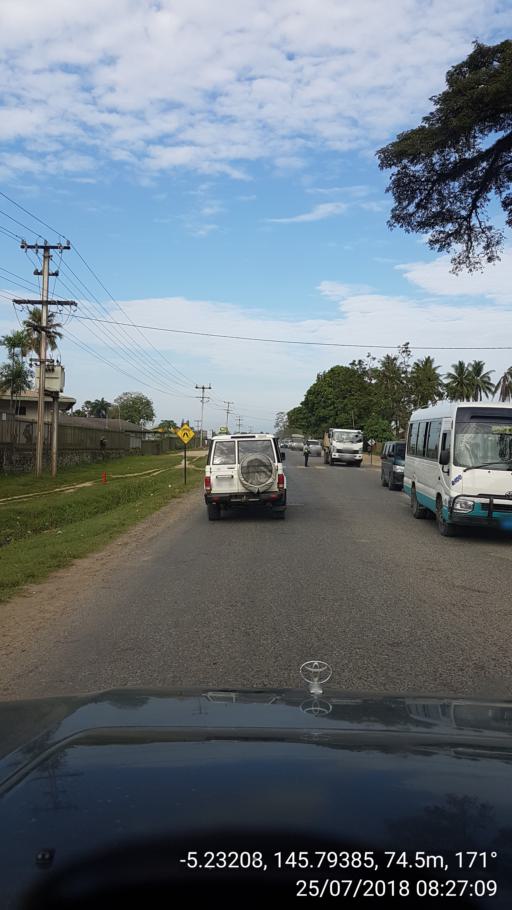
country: PG
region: Madang
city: Madang
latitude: -5.2319
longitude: 145.7938
